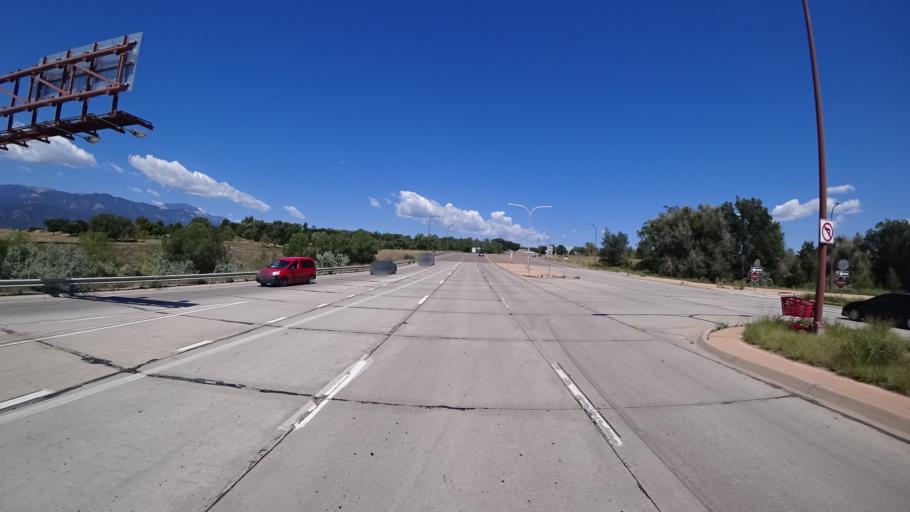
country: US
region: Colorado
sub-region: El Paso County
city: Colorado Springs
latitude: 38.8133
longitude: -104.7907
